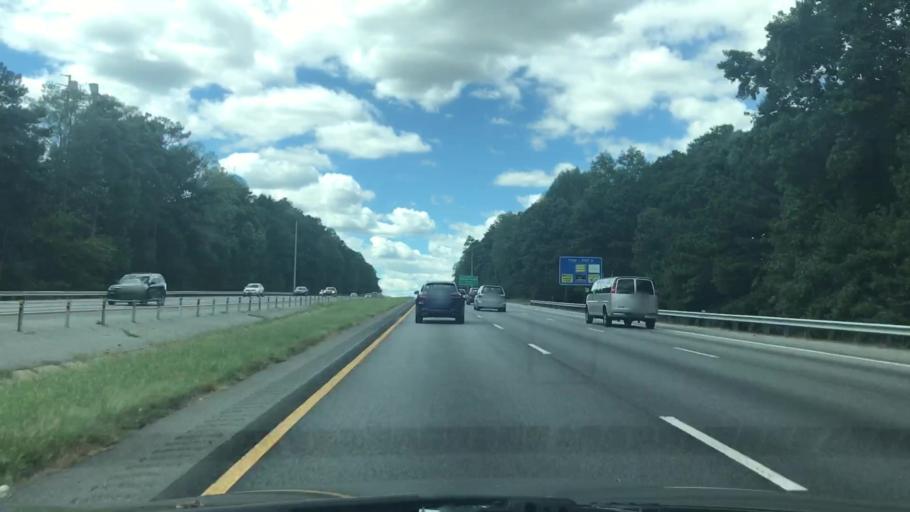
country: US
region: Georgia
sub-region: DeKalb County
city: Stone Mountain
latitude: 33.8324
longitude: -84.1859
